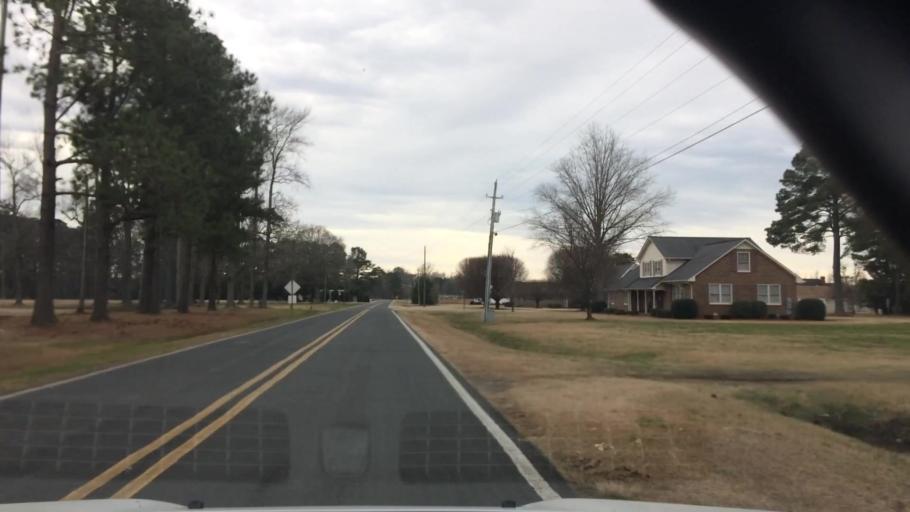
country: US
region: North Carolina
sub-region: Pitt County
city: Ayden
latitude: 35.4616
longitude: -77.3907
